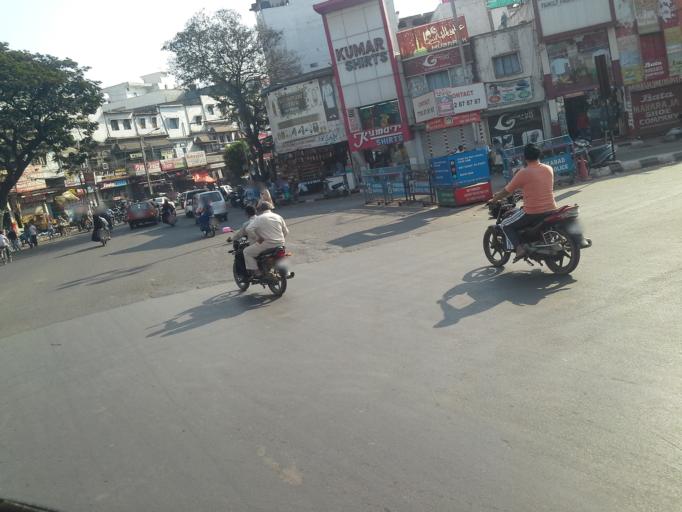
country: IN
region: Telangana
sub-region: Hyderabad
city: Hyderabad
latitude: 17.3707
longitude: 78.4770
